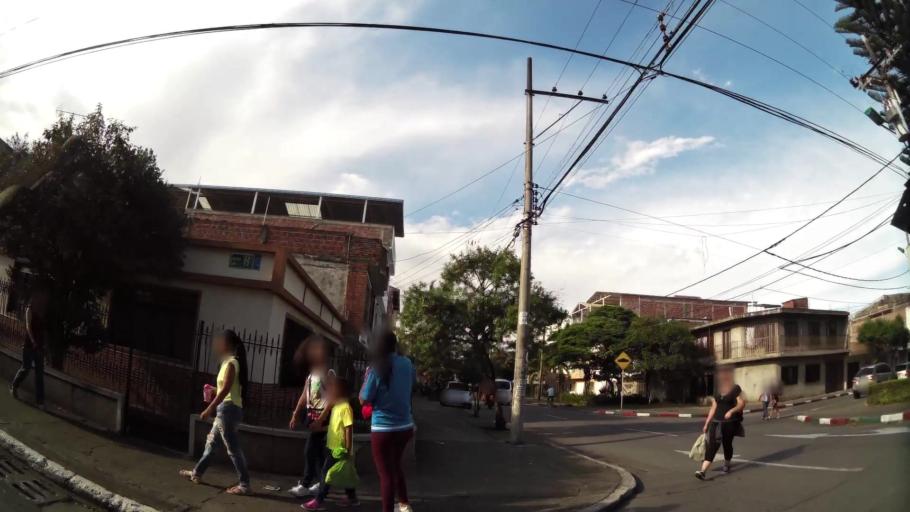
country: CO
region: Valle del Cauca
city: Cali
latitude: 3.4234
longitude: -76.5243
